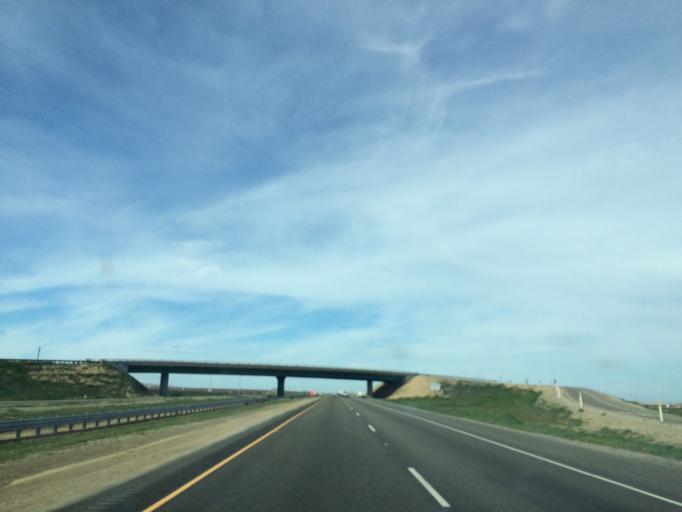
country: US
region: California
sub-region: Fresno County
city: Firebaugh
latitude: 36.6845
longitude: -120.6570
